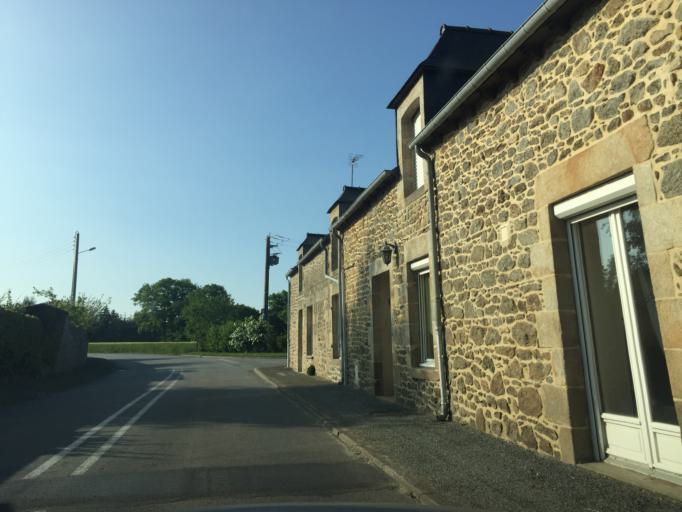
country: FR
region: Brittany
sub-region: Departement des Cotes-d'Armor
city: Crehen
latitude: 48.5505
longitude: -2.2328
